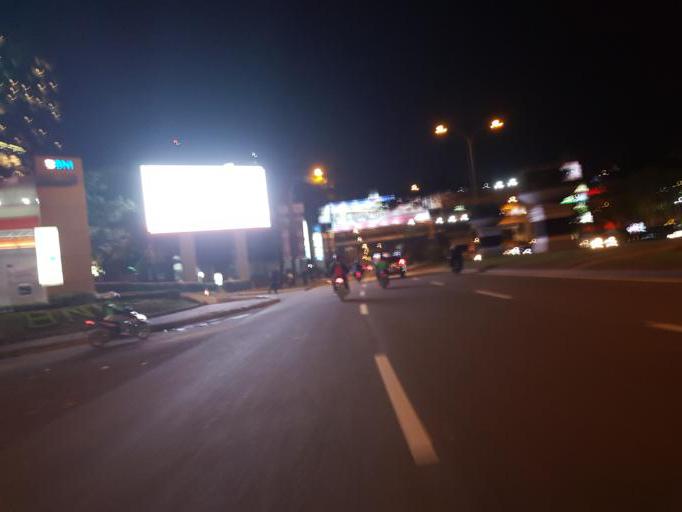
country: ID
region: West Java
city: Serpong
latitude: -6.2964
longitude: 106.6665
